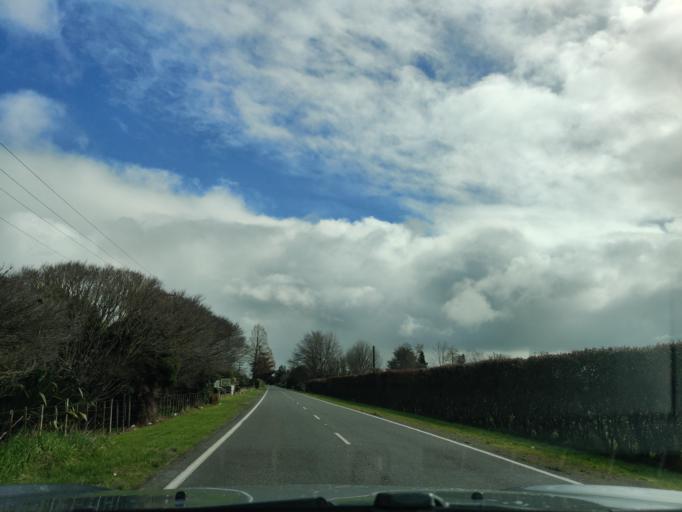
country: NZ
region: Hawke's Bay
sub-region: Hastings District
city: Hastings
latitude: -39.6782
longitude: 176.8577
